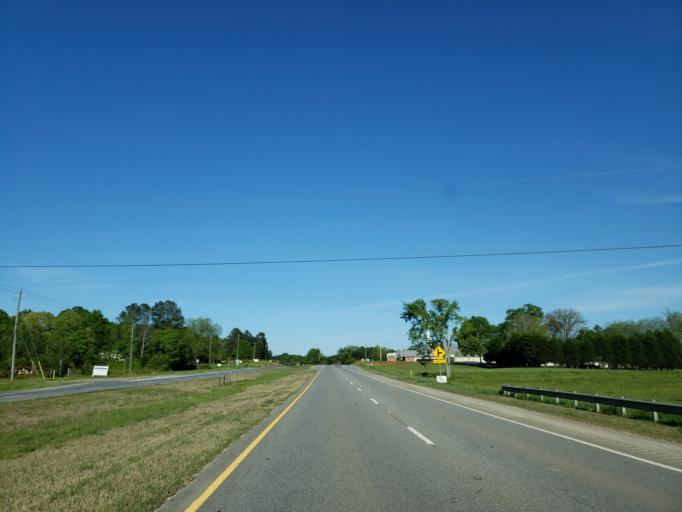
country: US
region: Georgia
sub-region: Polk County
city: Aragon
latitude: 34.0038
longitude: -85.1570
